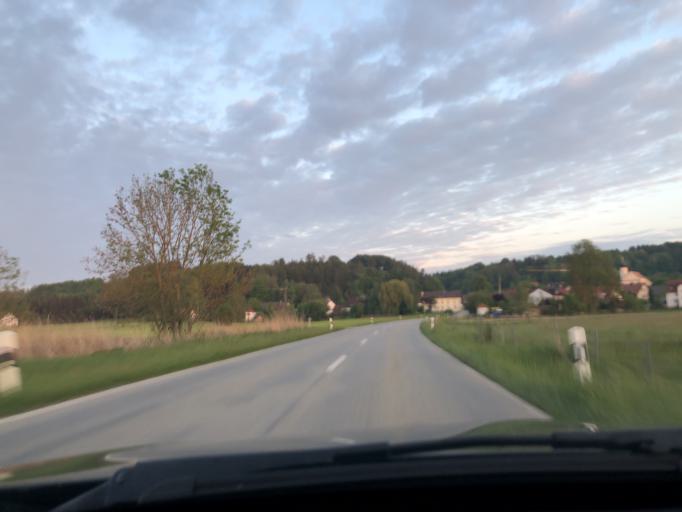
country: DE
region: Bavaria
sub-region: Upper Bavaria
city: Wolfersdorf
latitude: 48.4434
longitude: 11.7215
